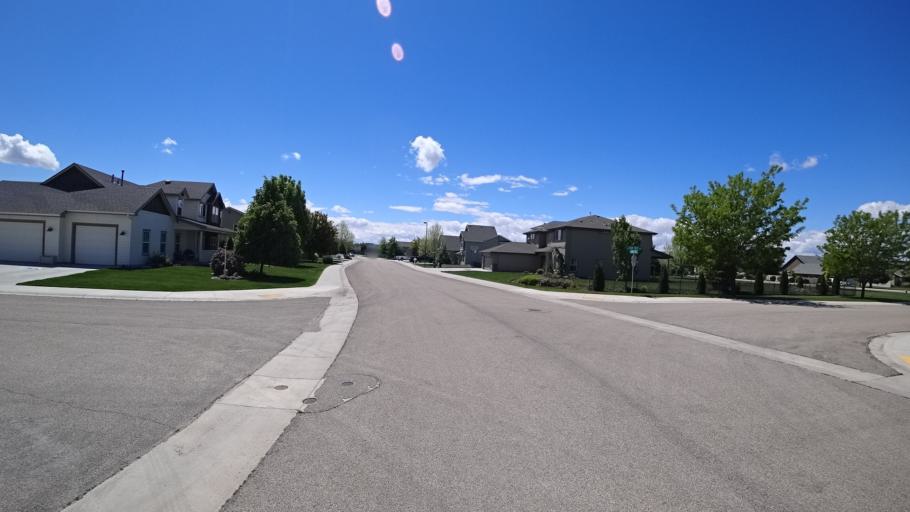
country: US
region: Idaho
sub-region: Ada County
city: Kuna
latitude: 43.5121
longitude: -116.4280
